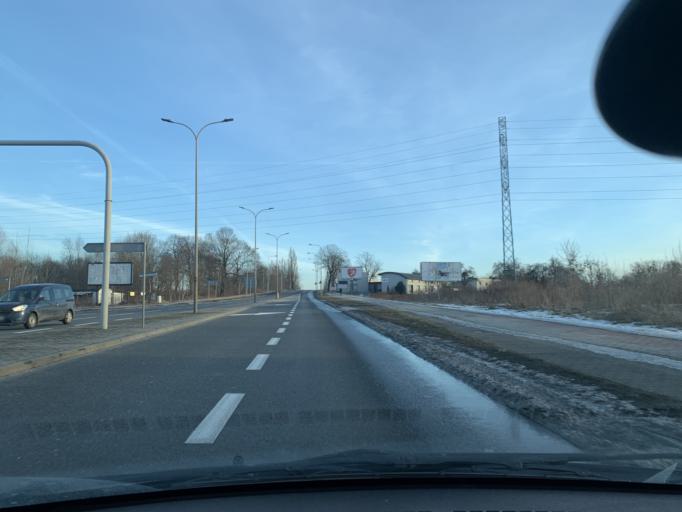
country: PL
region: Silesian Voivodeship
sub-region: Piekary Slaskie
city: Piekary Slaskie
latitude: 50.3665
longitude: 18.8985
